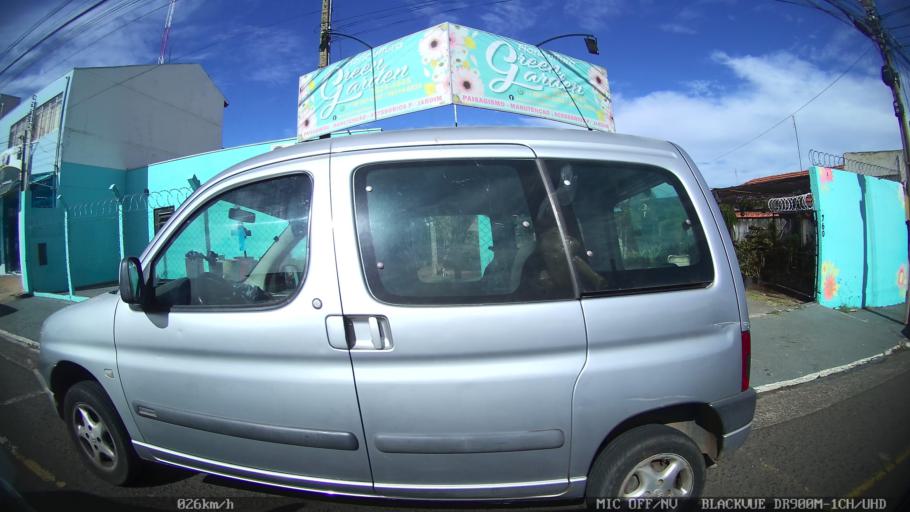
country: BR
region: Sao Paulo
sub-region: Catanduva
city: Catanduva
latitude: -21.1270
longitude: -48.9529
